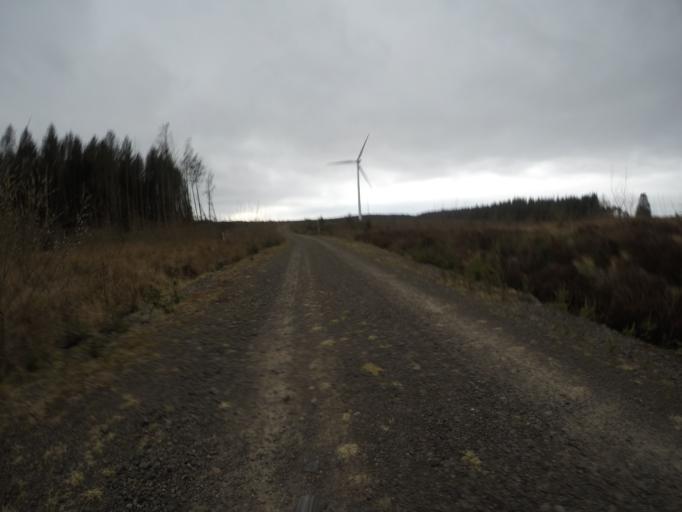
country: GB
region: Scotland
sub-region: East Ayrshire
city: Newmilns
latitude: 55.6780
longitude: -4.3484
